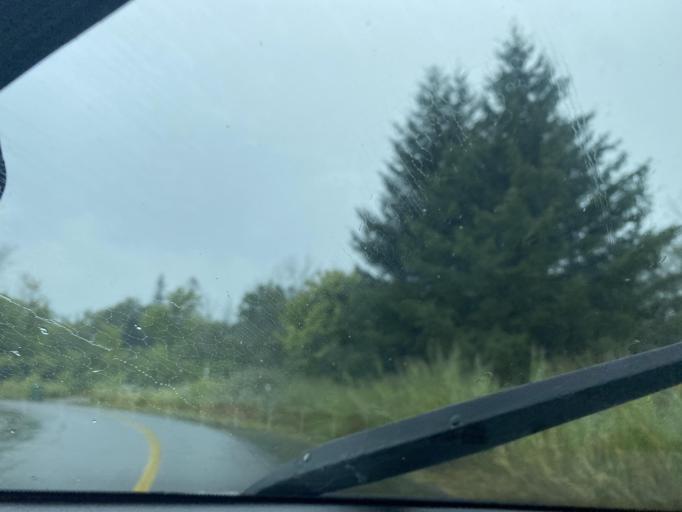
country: CA
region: Quebec
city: Baie-D'Urfe
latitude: 45.4670
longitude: -73.9231
